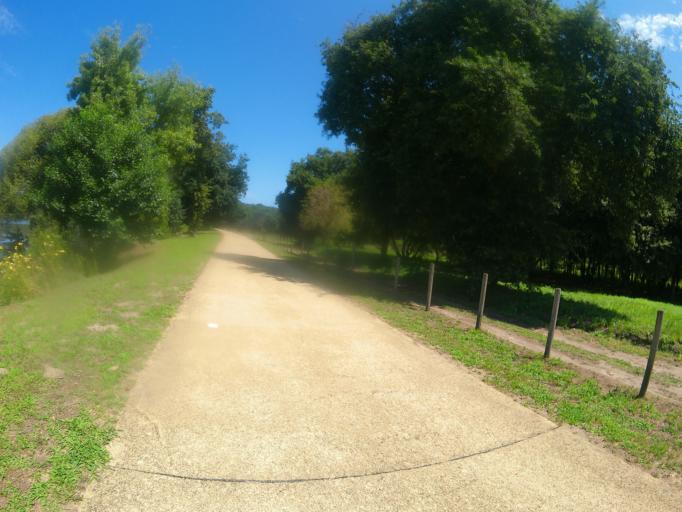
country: PT
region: Viana do Castelo
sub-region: Vila Nova de Cerveira
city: Vila Nova de Cerveira
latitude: 41.9611
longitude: -8.7442
